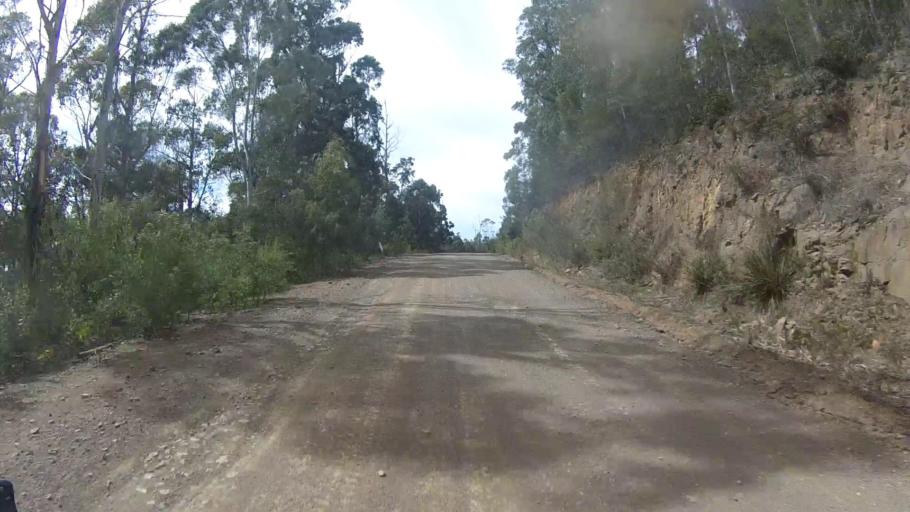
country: AU
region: Tasmania
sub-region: Sorell
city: Sorell
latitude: -42.7540
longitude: 147.8287
